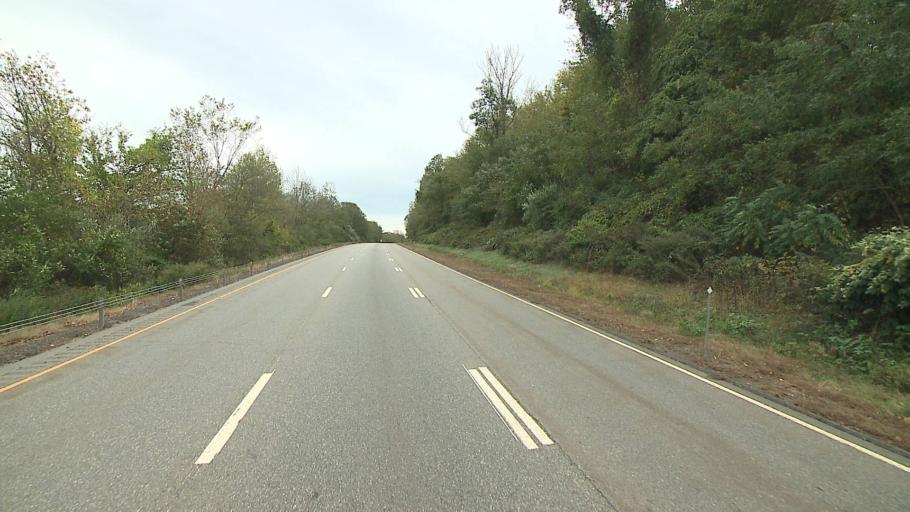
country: US
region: Connecticut
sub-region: Middlesex County
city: Deep River Center
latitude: 41.3791
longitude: -72.4426
